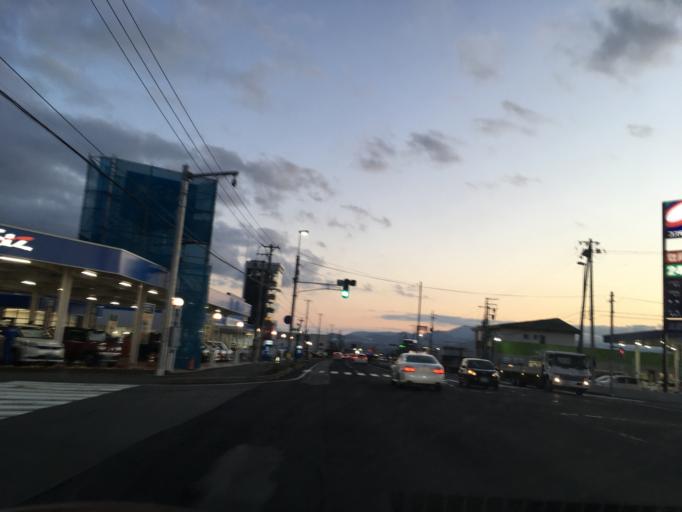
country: JP
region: Yamagata
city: Yamagata-shi
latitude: 38.2222
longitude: 140.3329
